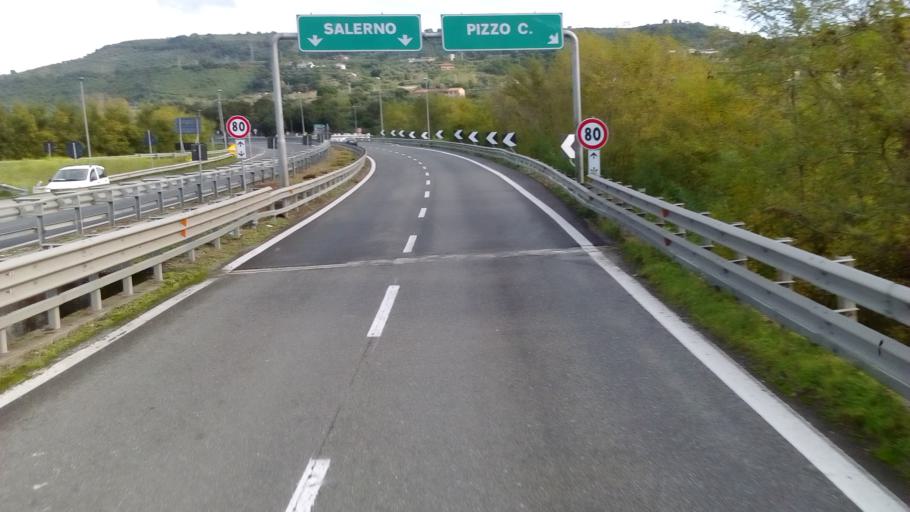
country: IT
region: Calabria
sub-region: Provincia di Vibo-Valentia
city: Pizzo
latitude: 38.7710
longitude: 16.2120
